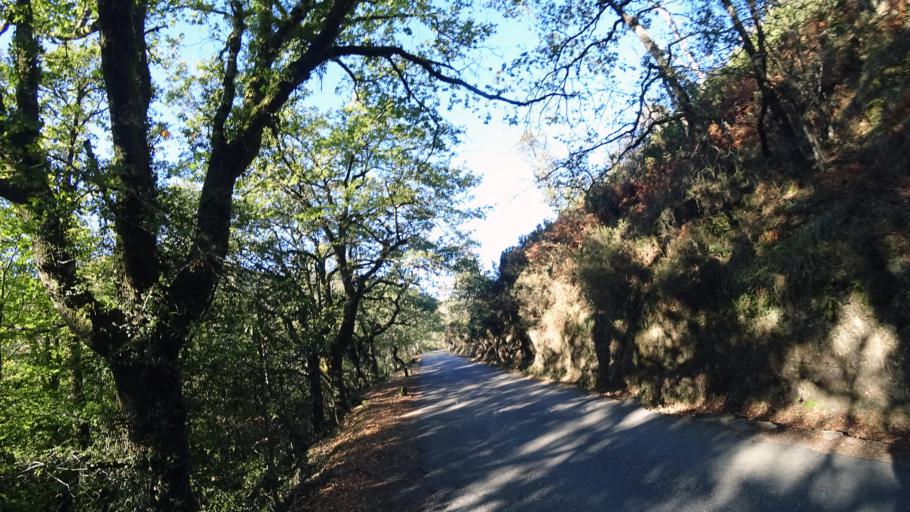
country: ES
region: Galicia
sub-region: Provincia de Ourense
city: Lobios
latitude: 41.7955
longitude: -8.1342
